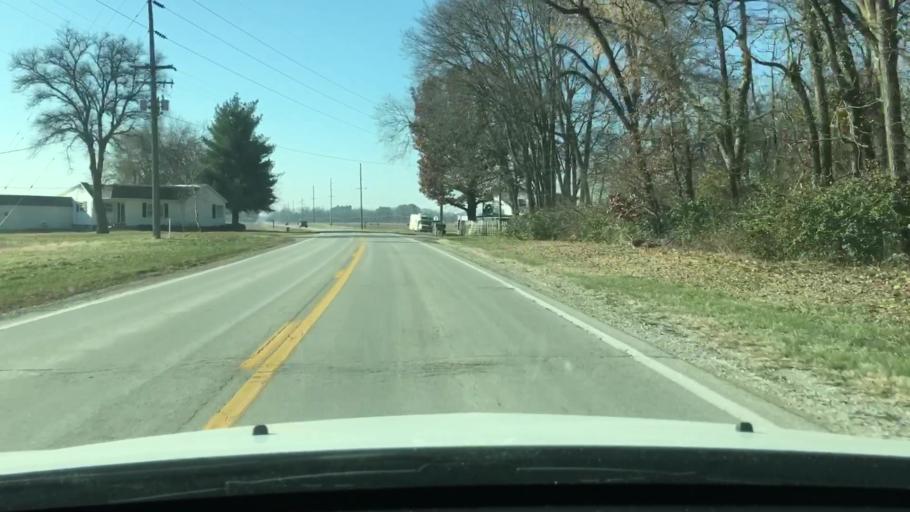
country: US
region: Illinois
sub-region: Cass County
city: Beardstown
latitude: 39.9783
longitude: -90.4552
